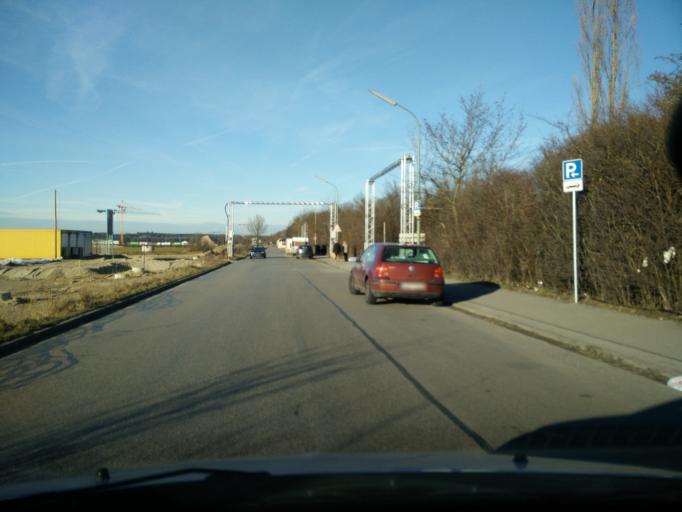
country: DE
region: Bavaria
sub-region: Upper Bavaria
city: Grafelfing
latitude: 48.1422
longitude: 11.4114
